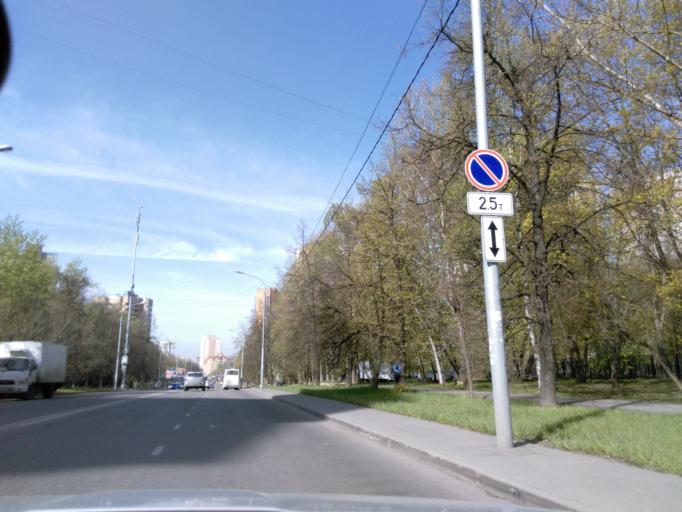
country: RU
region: Moscow
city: Novokhovrino
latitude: 55.8607
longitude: 37.4985
